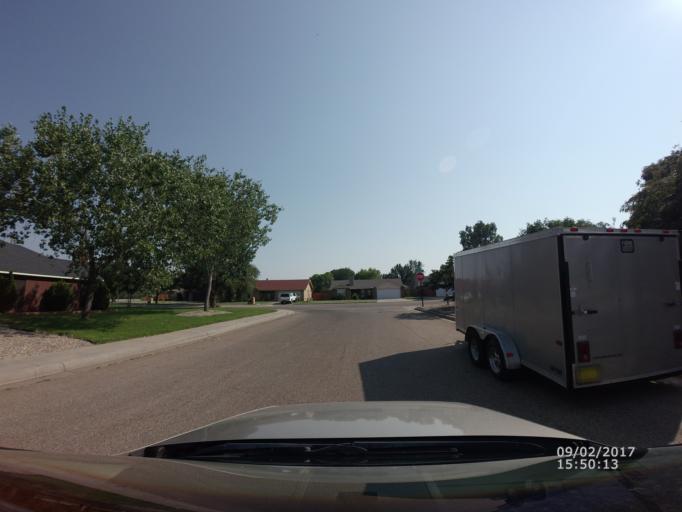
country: US
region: New Mexico
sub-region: Curry County
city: Clovis
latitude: 34.4461
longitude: -103.1792
